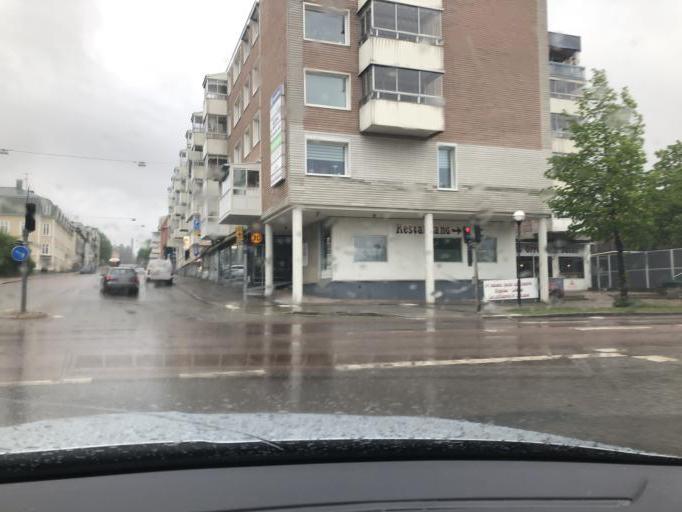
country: SE
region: Vaesternorrland
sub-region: OErnskoeldsviks Kommun
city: Ornskoldsvik
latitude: 63.2912
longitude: 18.7162
